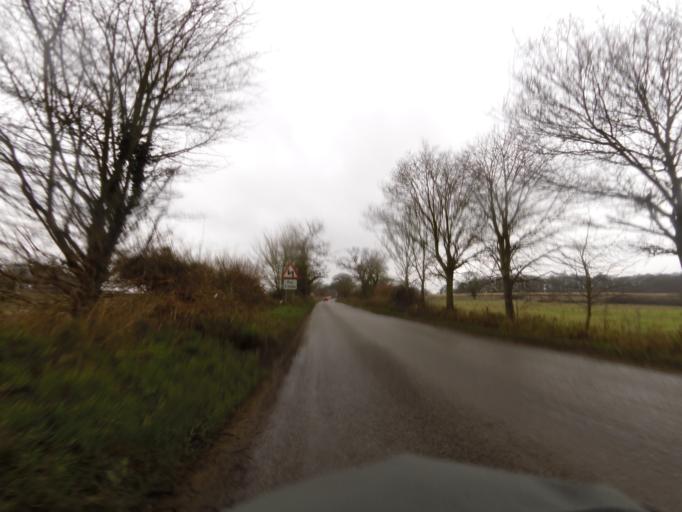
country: GB
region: England
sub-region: Norfolk
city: Briston
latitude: 52.8818
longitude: 1.0795
